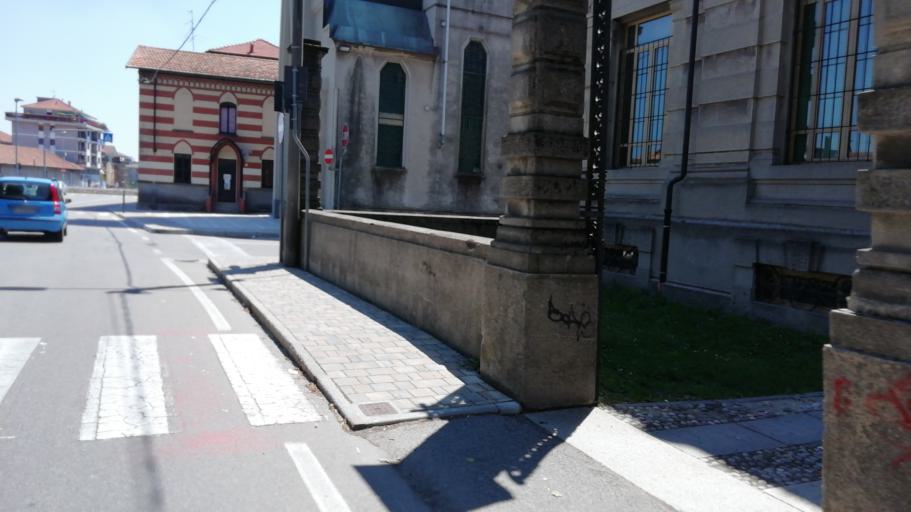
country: IT
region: Piedmont
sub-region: Provincia di Novara
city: Borgomanero
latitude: 45.6994
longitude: 8.4579
